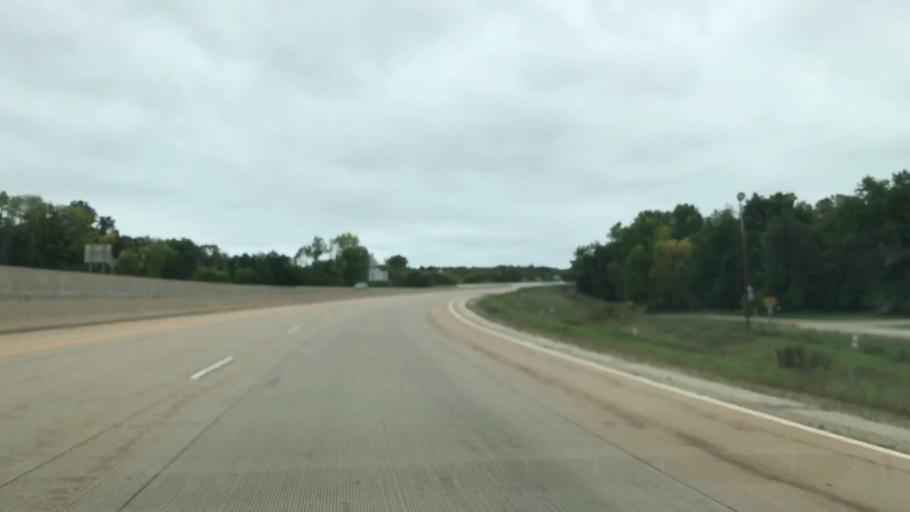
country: US
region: Wisconsin
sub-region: Oconto County
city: Oconto
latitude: 44.8896
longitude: -87.8952
